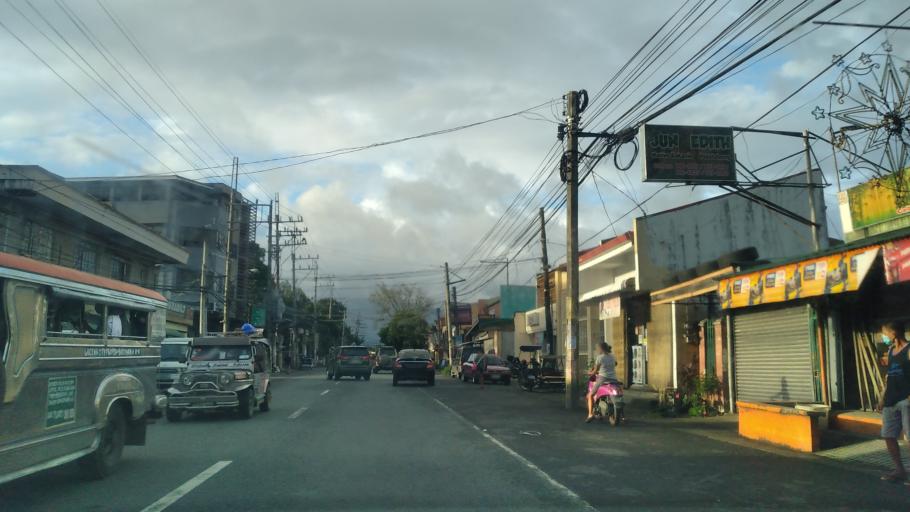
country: PH
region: Calabarzon
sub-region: Province of Quezon
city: Lucena
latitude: 13.9523
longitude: 121.6125
